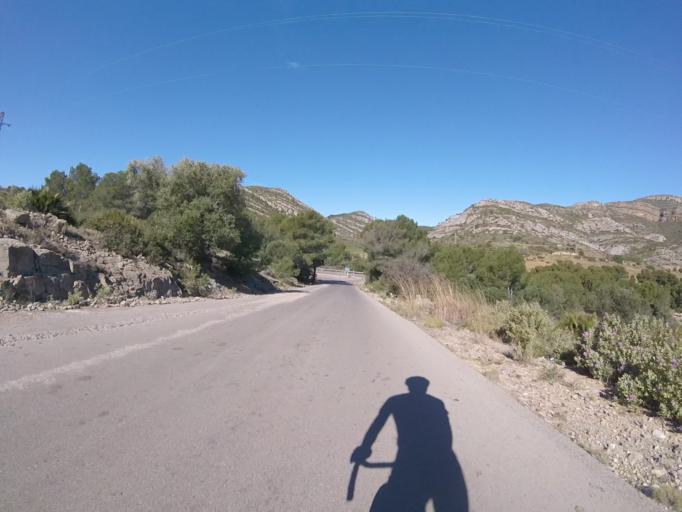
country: ES
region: Valencia
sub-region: Provincia de Castello
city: Orpesa/Oropesa del Mar
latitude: 40.0740
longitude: 0.1117
